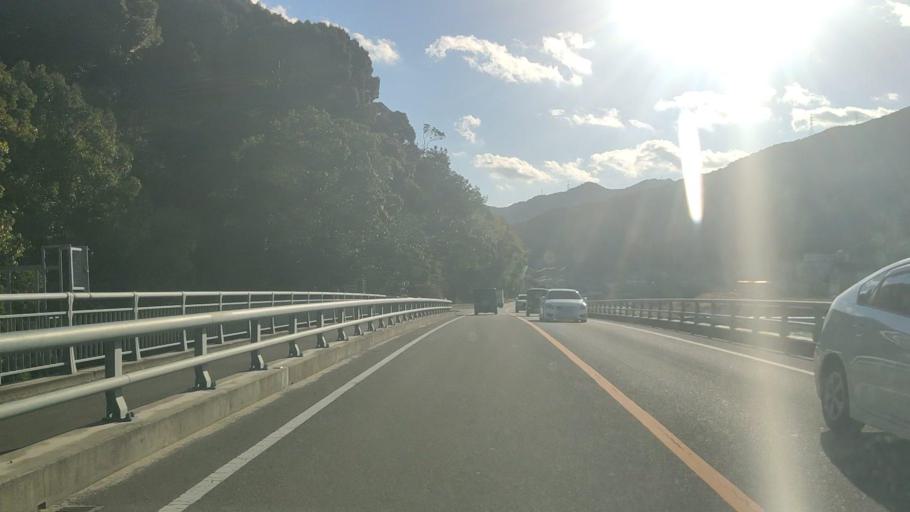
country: JP
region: Saga Prefecture
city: Saga-shi
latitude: 33.3586
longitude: 130.2528
